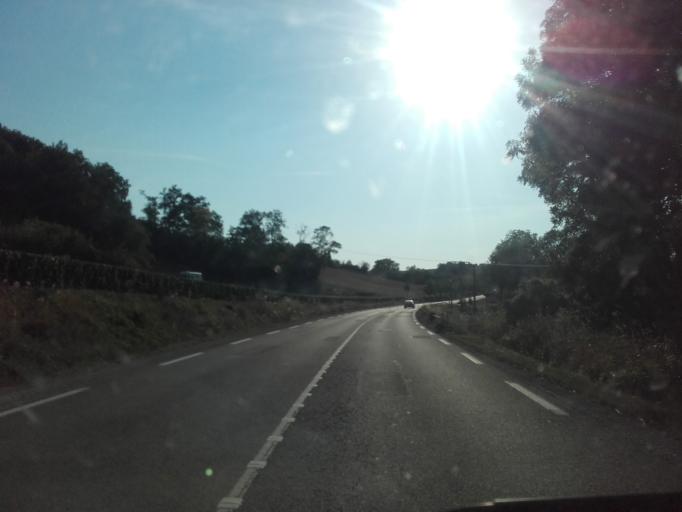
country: FR
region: Bourgogne
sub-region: Departement de l'Yonne
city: Chablis
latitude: 47.8179
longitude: 3.7322
